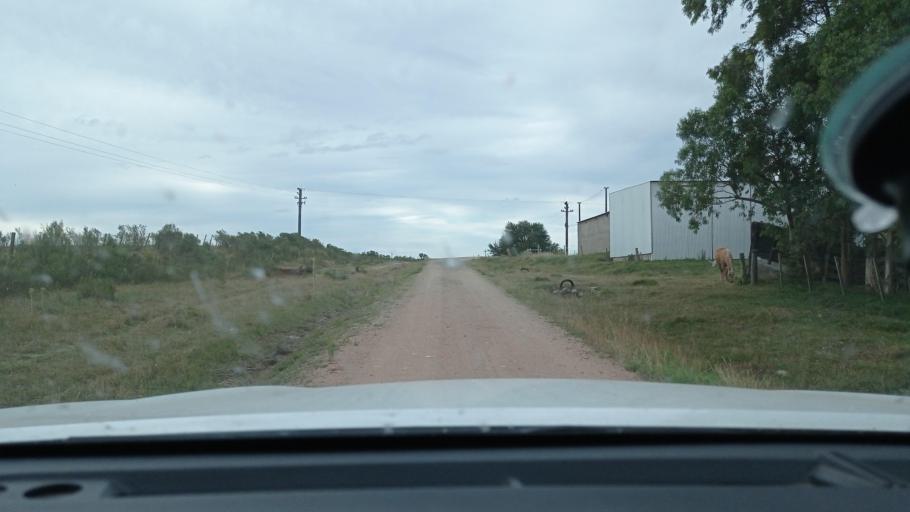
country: UY
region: Florida
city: Casupa
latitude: -34.1191
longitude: -55.7701
